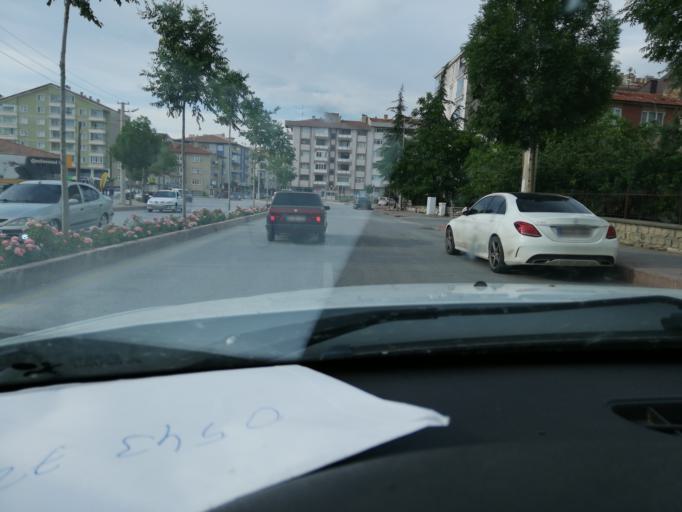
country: TR
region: Kirsehir
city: Kirsehir
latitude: 39.1391
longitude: 34.1604
